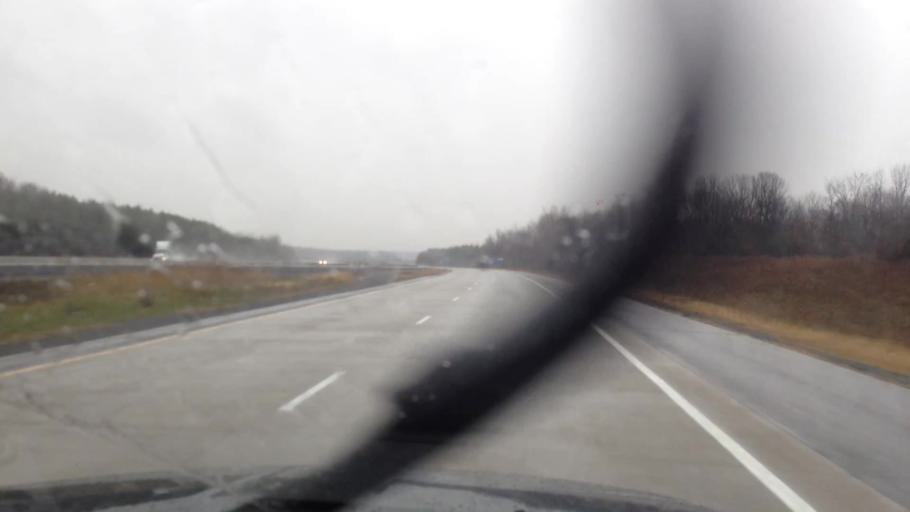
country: CA
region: Ontario
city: Hawkesbury
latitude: 45.4490
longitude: -74.7080
